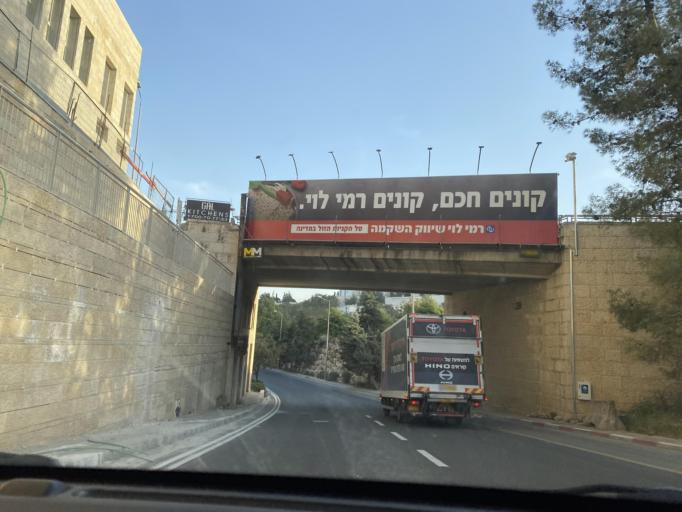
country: IL
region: Jerusalem
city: Jerusalem
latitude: 31.7662
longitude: 35.1928
